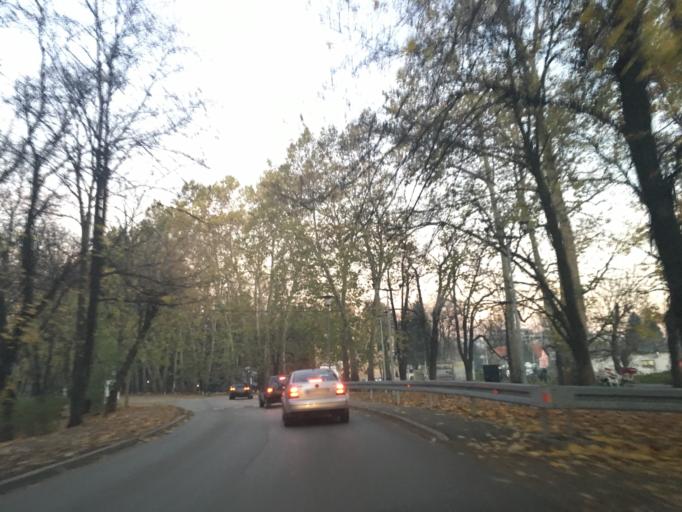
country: BA
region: Federation of Bosnia and Herzegovina
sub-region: Kanton Sarajevo
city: Sarajevo
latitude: 43.8247
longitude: 18.3022
